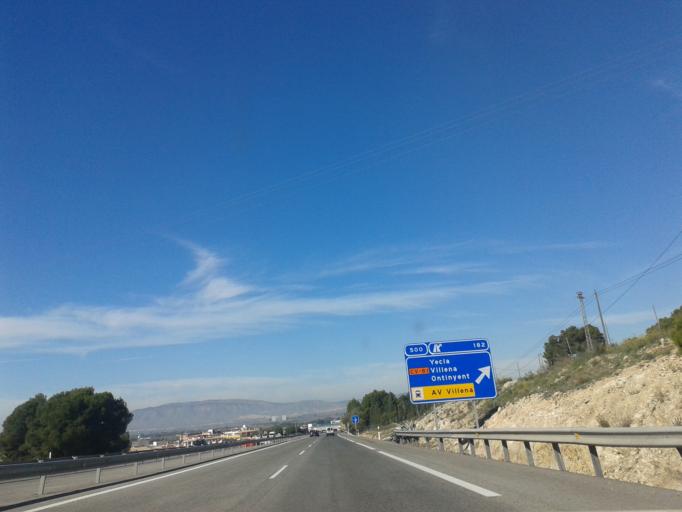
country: ES
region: Valencia
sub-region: Provincia de Alicante
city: Villena
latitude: 38.6394
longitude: -0.8608
